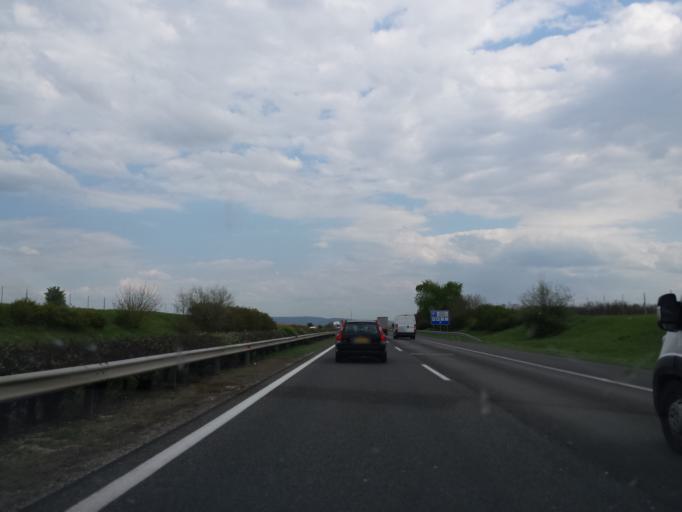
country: HU
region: Komarom-Esztergom
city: Kocs
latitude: 47.6370
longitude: 18.2347
